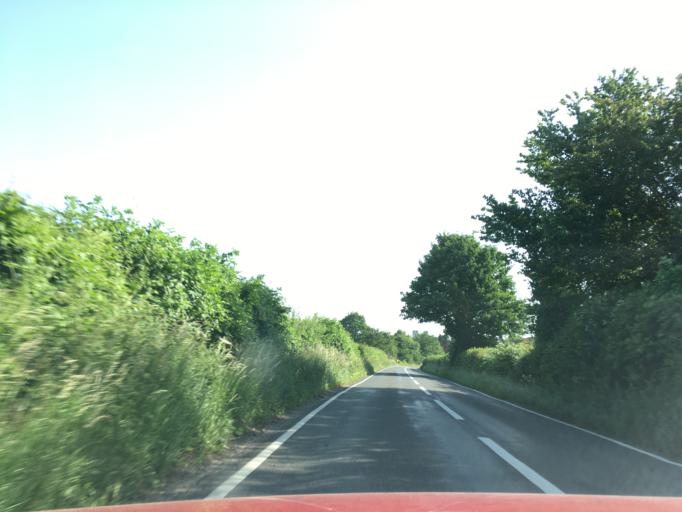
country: GB
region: England
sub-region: Oxfordshire
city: Stonesfield
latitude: 51.9248
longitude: -1.4054
